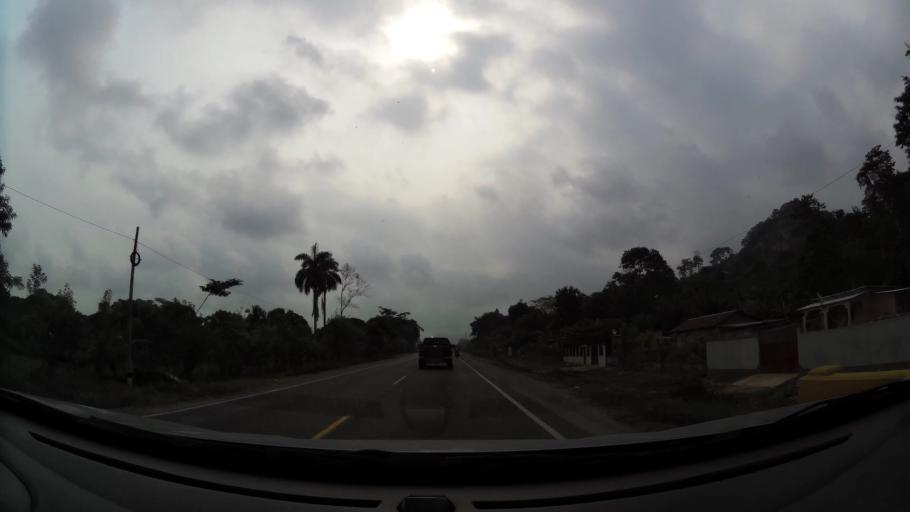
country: HN
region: Yoro
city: Guaimitas
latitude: 15.4933
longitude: -87.7434
